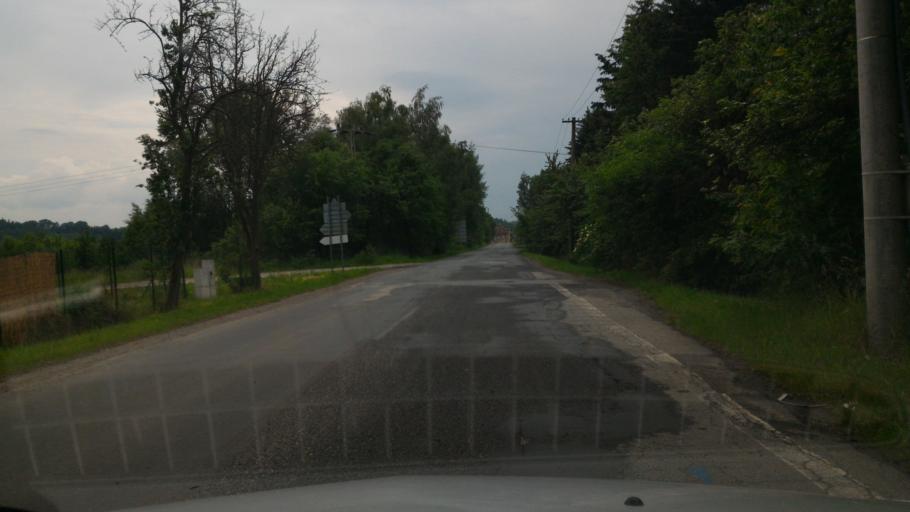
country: CZ
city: Jablonne v Podjestedi
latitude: 50.7737
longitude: 14.7687
